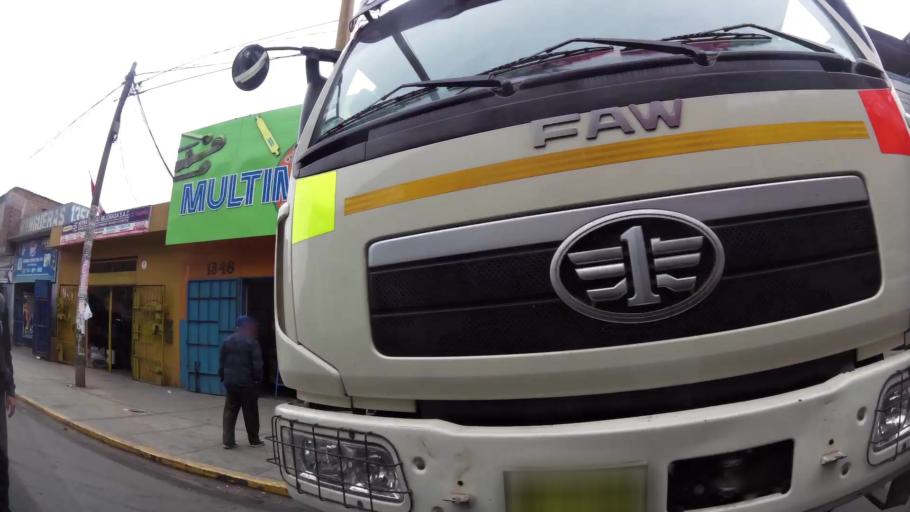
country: PE
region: Lima
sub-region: Lima
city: San Luis
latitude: -12.0750
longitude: -77.0113
